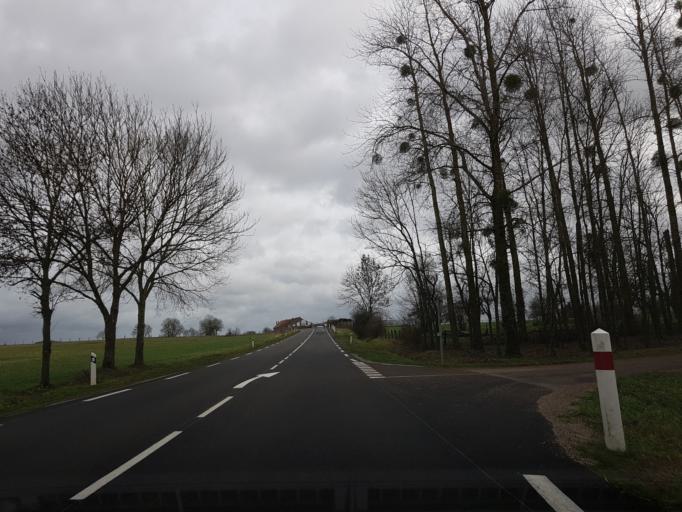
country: FR
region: Champagne-Ardenne
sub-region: Departement de la Haute-Marne
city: Chalindrey
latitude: 47.8510
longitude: 5.4101
